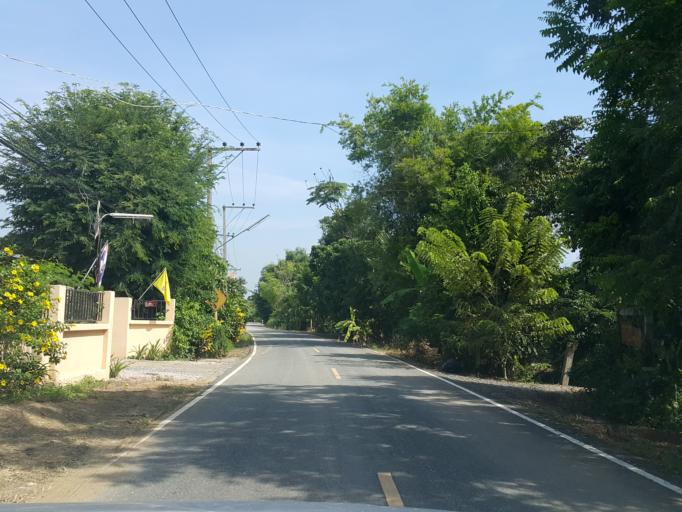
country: TH
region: Chiang Mai
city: Saraphi
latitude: 18.6861
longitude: 99.0751
